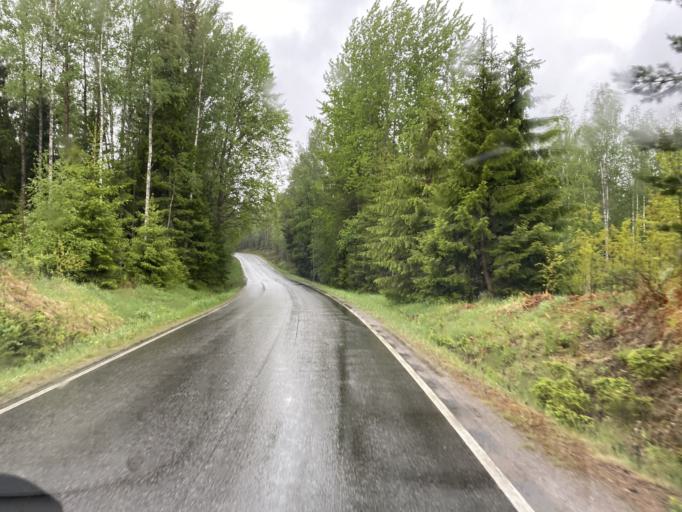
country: FI
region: Haeme
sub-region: Forssa
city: Humppila
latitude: 61.0784
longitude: 23.3110
